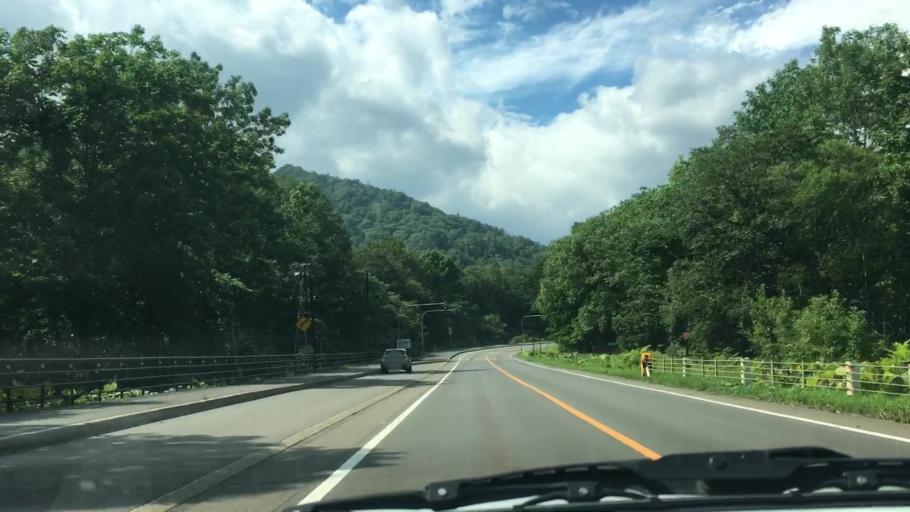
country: JP
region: Hokkaido
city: Otofuke
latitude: 43.3557
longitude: 143.2576
